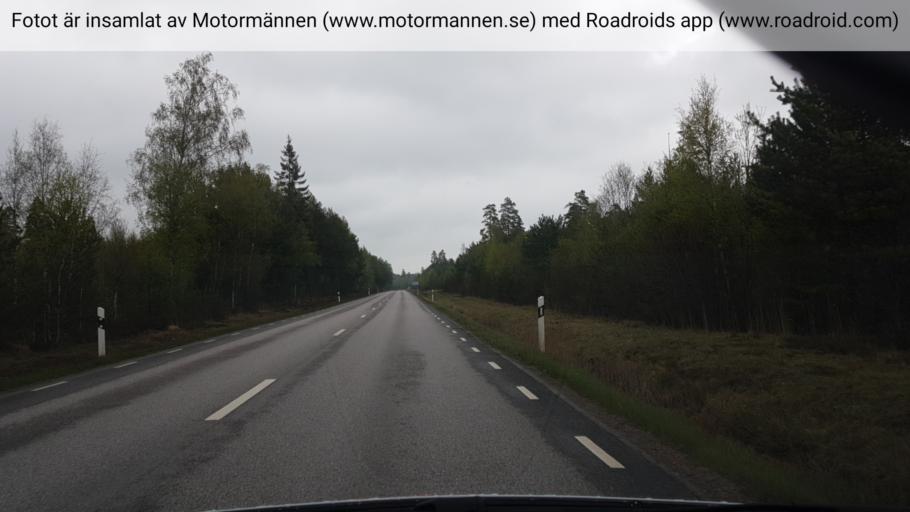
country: SE
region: Vaestra Goetaland
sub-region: Skovde Kommun
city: Stopen
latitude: 58.4475
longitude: 13.9437
